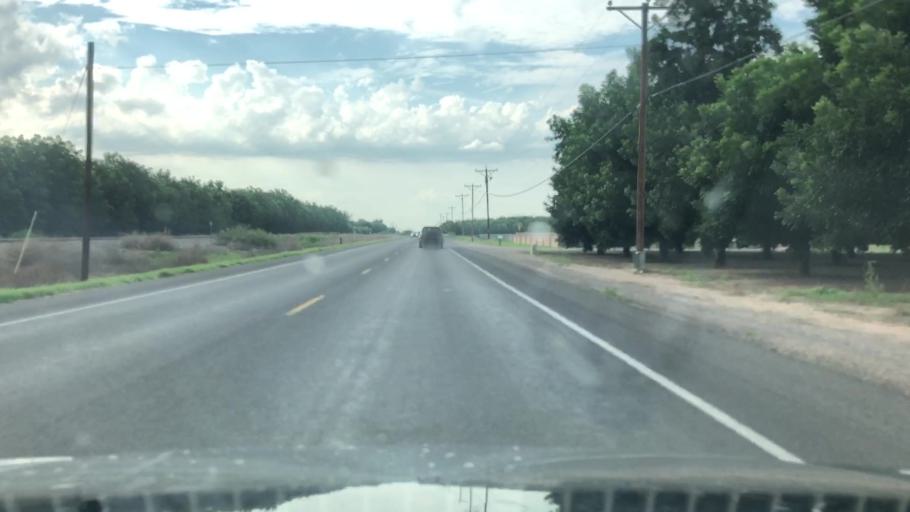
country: US
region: New Mexico
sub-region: Dona Ana County
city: San Miguel
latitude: 32.2170
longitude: -106.7296
